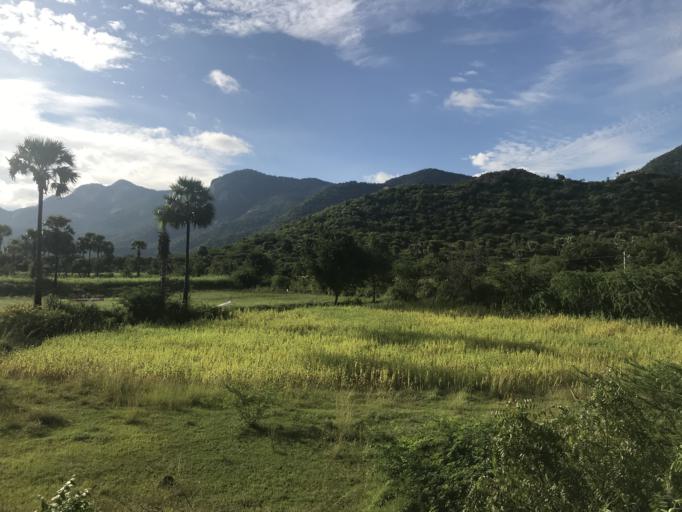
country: IN
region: Tamil Nadu
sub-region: Coimbatore
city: Madukkarai
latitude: 10.8912
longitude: 76.8811
